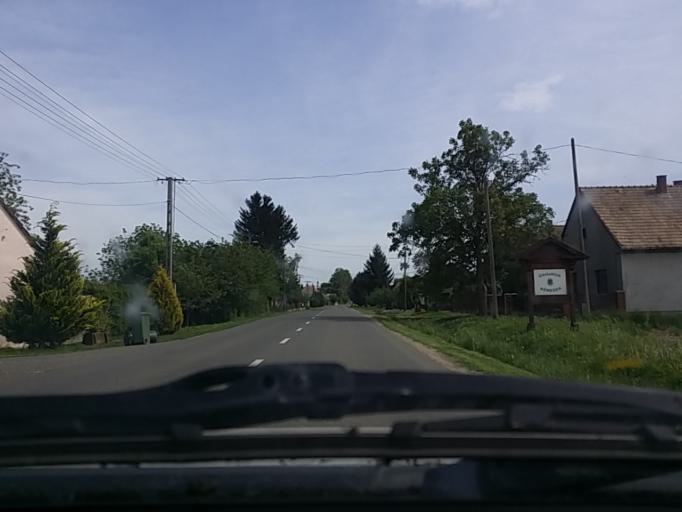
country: HR
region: Osjecko-Baranjska
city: Viljevo
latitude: 45.8290
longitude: 18.0955
